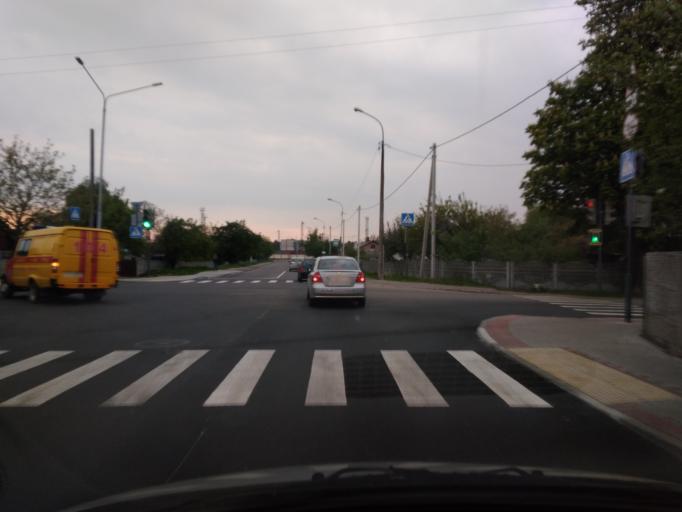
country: BY
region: Brest
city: Brest
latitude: 52.1059
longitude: 23.7157
